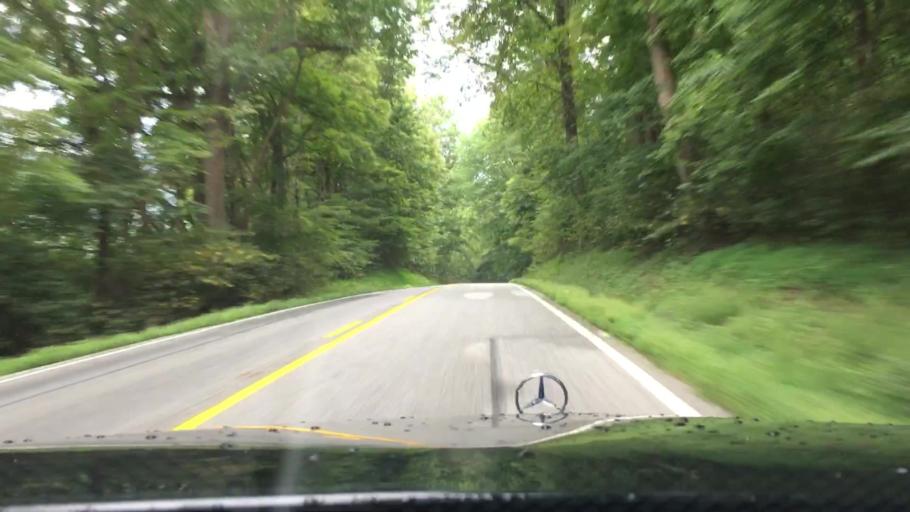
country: US
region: Virginia
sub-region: Nelson County
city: Nellysford
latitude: 37.8438
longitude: -78.9274
